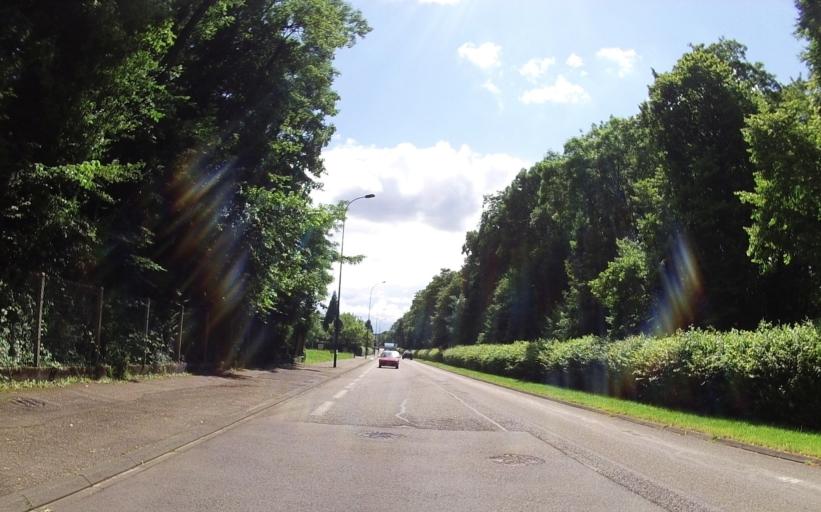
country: FR
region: Alsace
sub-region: Departement du Bas-Rhin
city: Reichshoffen
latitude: 48.9274
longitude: 7.6660
